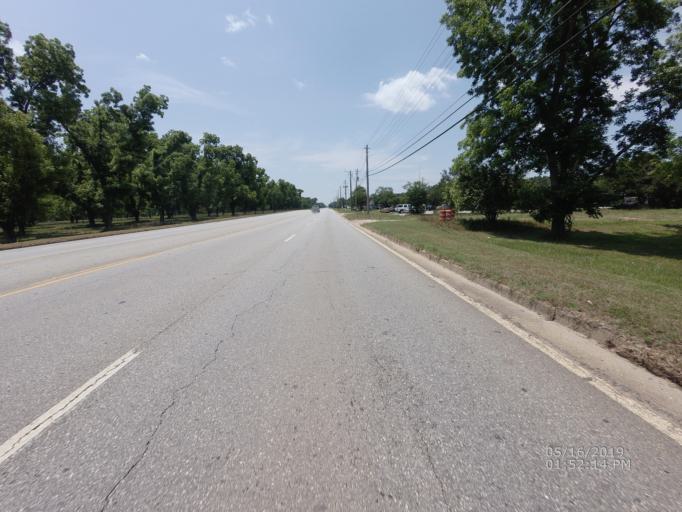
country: US
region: Georgia
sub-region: Dougherty County
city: Albany
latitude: 31.5491
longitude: -84.2136
